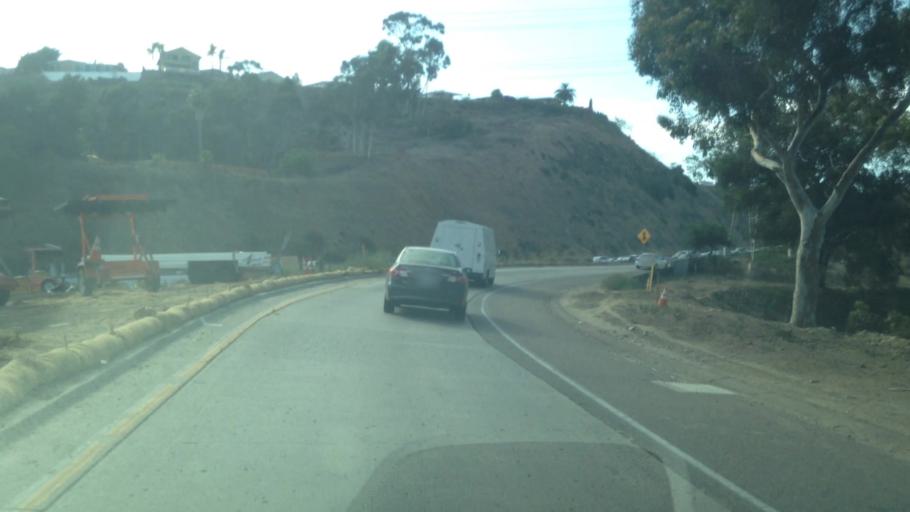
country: US
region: California
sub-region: San Diego County
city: San Diego
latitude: 32.7730
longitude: -117.1600
